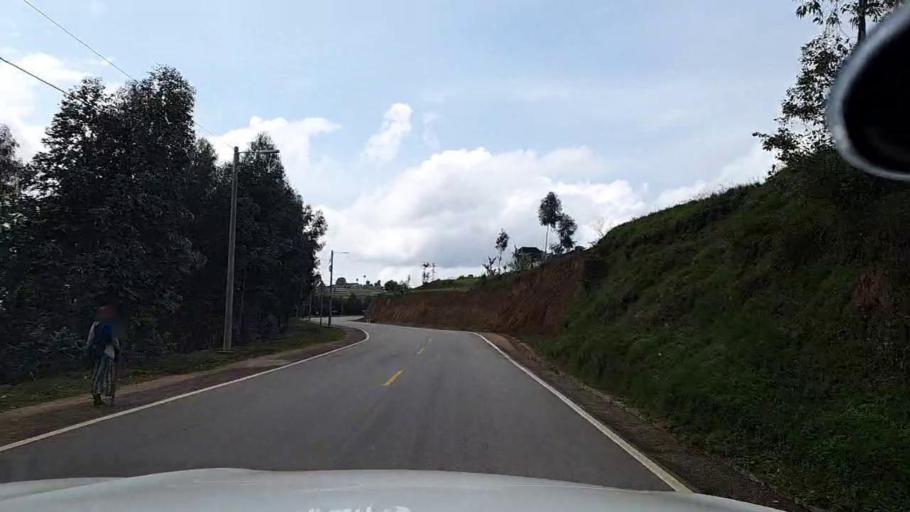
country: RW
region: Southern Province
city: Nzega
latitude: -2.5221
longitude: 29.4539
